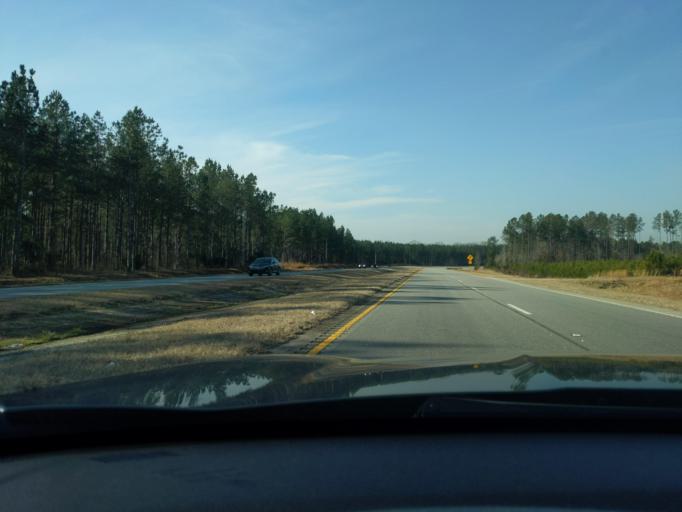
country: US
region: South Carolina
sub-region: Abbeville County
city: Abbeville
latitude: 34.1154
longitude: -82.4650
